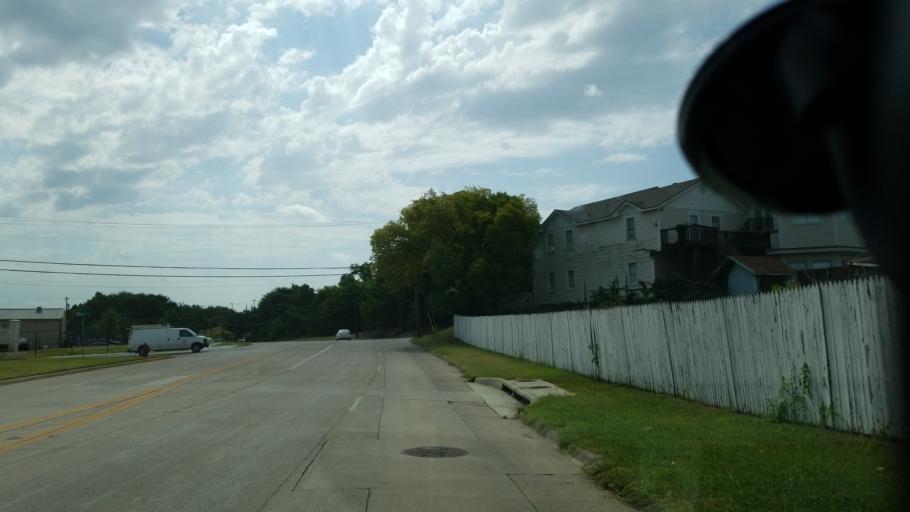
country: US
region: Texas
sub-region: Dallas County
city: Grand Prairie
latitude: 32.7491
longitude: -96.9989
